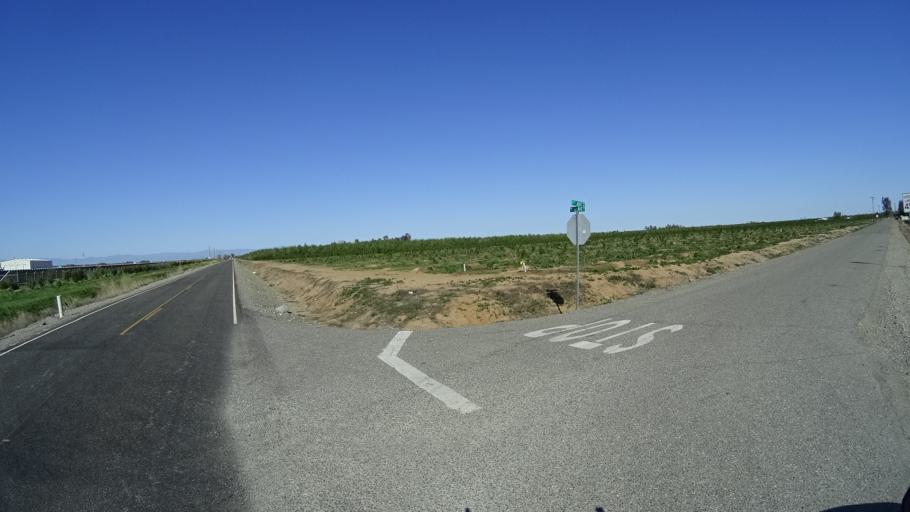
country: US
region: California
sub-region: Glenn County
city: Hamilton City
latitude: 39.7665
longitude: -122.0477
